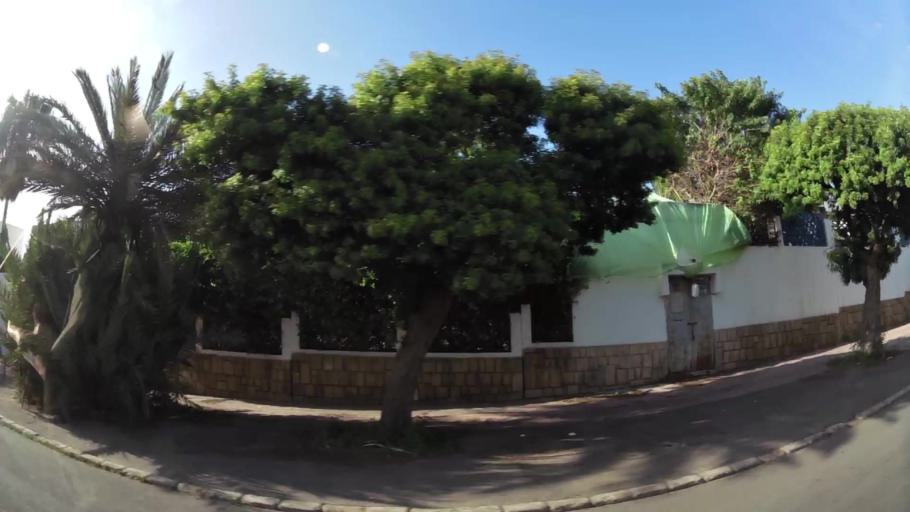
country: MA
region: Souss-Massa-Draa
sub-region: Agadir-Ida-ou-Tnan
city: Agadir
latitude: 30.4272
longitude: -9.5895
